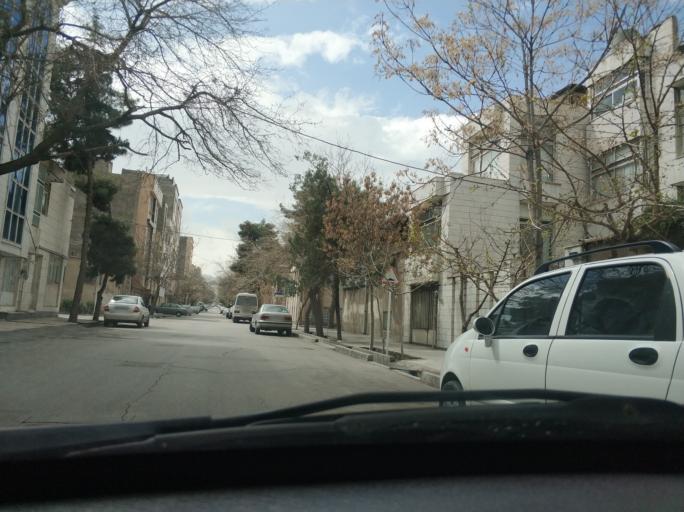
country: IR
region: Razavi Khorasan
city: Mashhad
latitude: 36.2789
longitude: 59.5729
